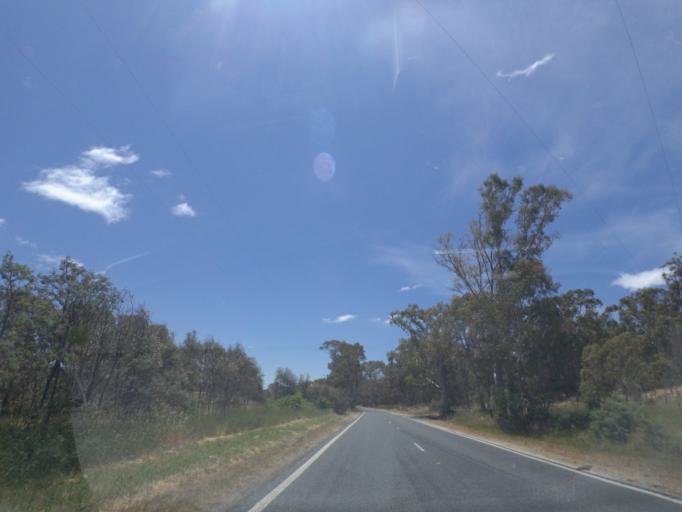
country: AU
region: Victoria
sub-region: Mount Alexander
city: Castlemaine
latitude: -37.1858
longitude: 144.1484
